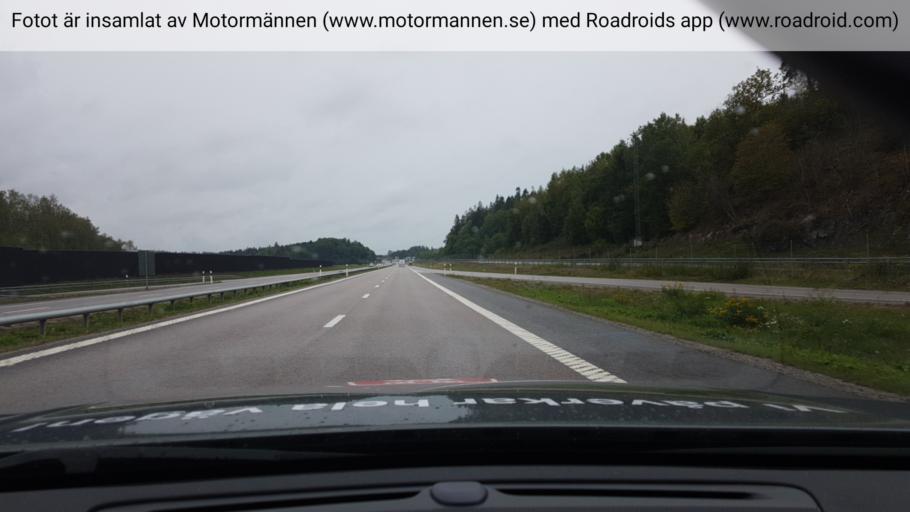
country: SE
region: Stockholm
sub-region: Nynashamns Kommun
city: Osmo
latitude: 58.9761
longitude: 17.9115
